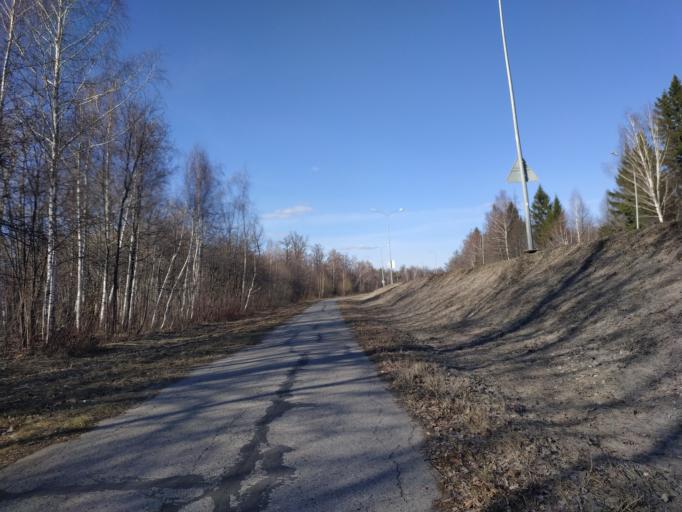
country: RU
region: Chuvashia
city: Ishley
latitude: 56.1225
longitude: 47.0605
